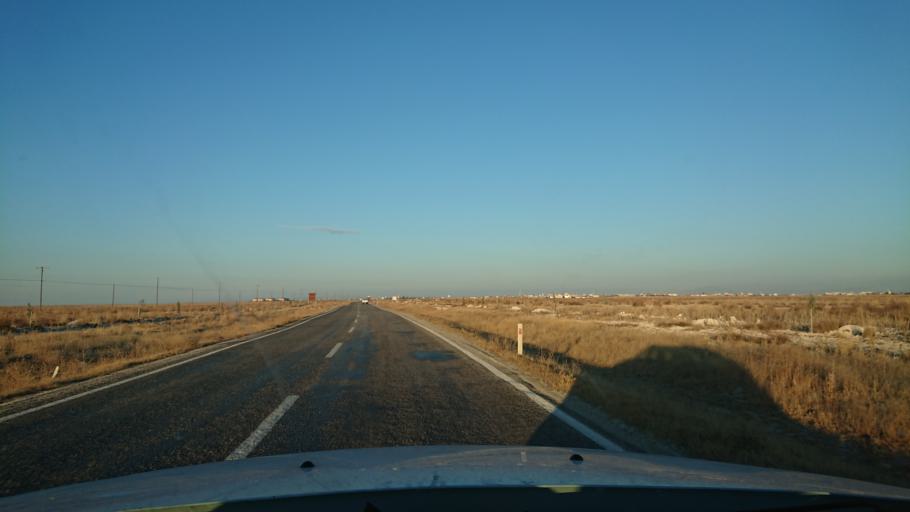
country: TR
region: Aksaray
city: Eskil
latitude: 38.3814
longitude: 33.3768
